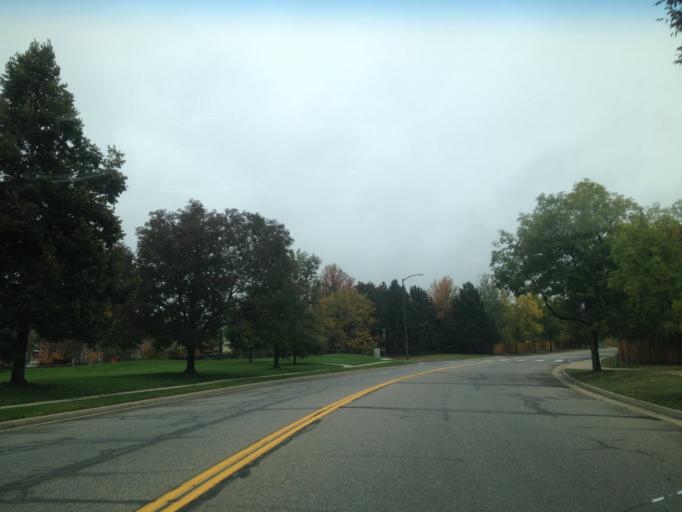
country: US
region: Colorado
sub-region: Boulder County
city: Louisville
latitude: 39.9748
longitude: -105.1526
